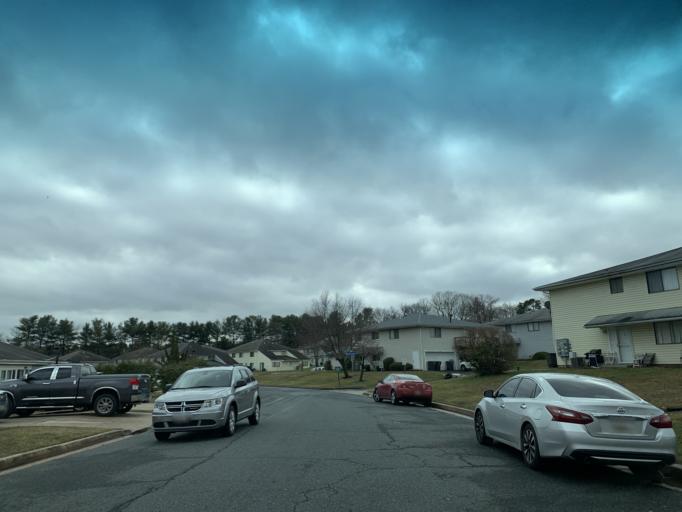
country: US
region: Maryland
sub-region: Harford County
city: Edgewood
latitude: 39.4279
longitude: -76.3194
